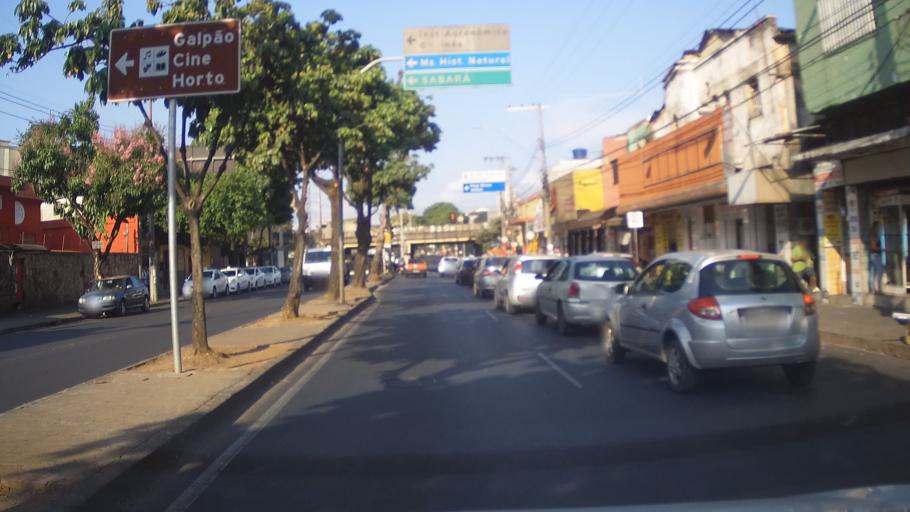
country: BR
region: Minas Gerais
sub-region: Belo Horizonte
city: Belo Horizonte
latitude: -19.9089
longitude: -43.9145
